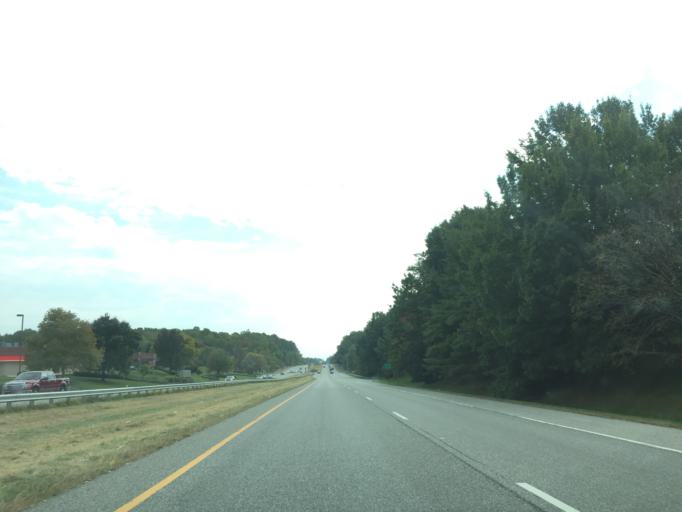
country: US
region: Maryland
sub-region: Harford County
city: Bel Air South
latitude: 39.4955
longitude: -76.3289
